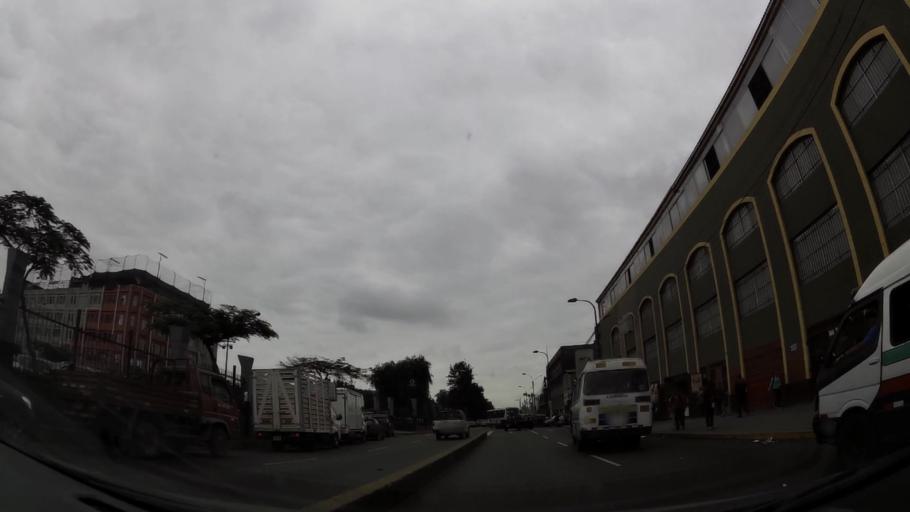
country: PE
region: Lima
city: Lima
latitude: -12.0434
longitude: -77.0441
